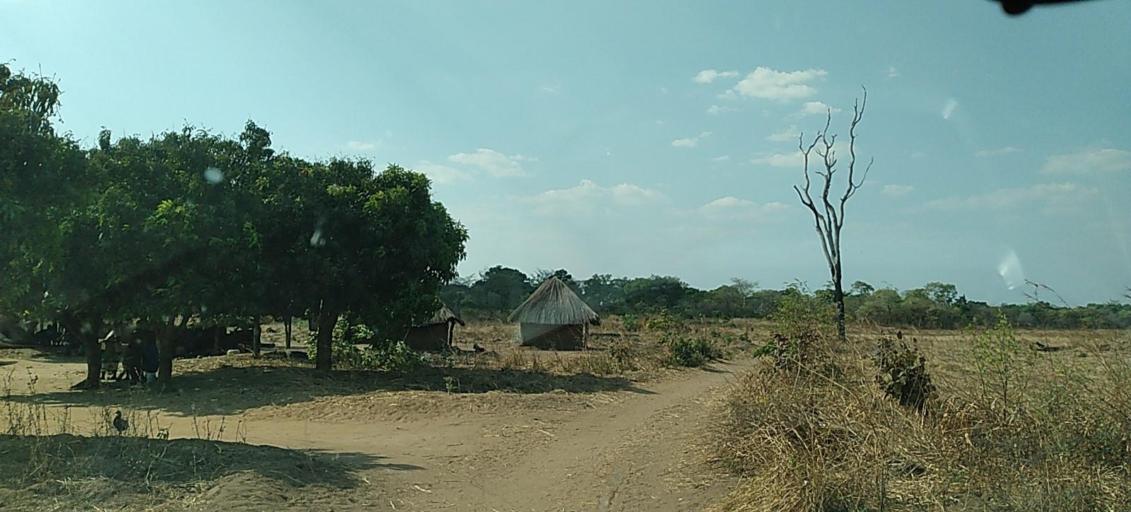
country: ZM
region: North-Western
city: Kalengwa
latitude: -13.0581
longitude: 24.9552
